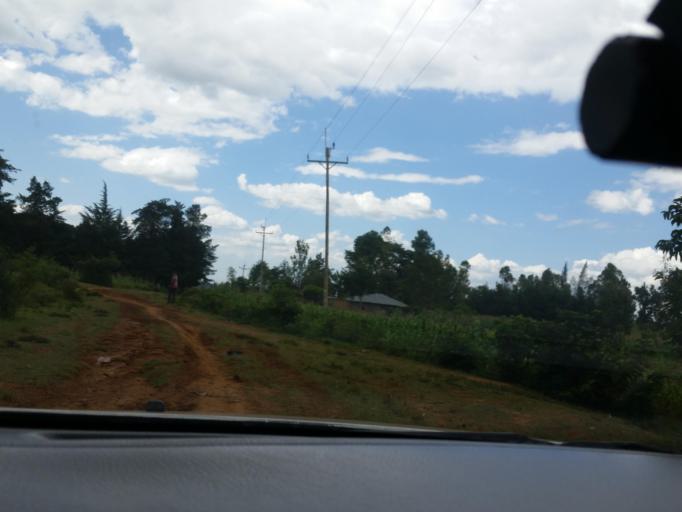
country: KE
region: Siaya
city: Yala
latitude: 0.1082
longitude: 34.4112
